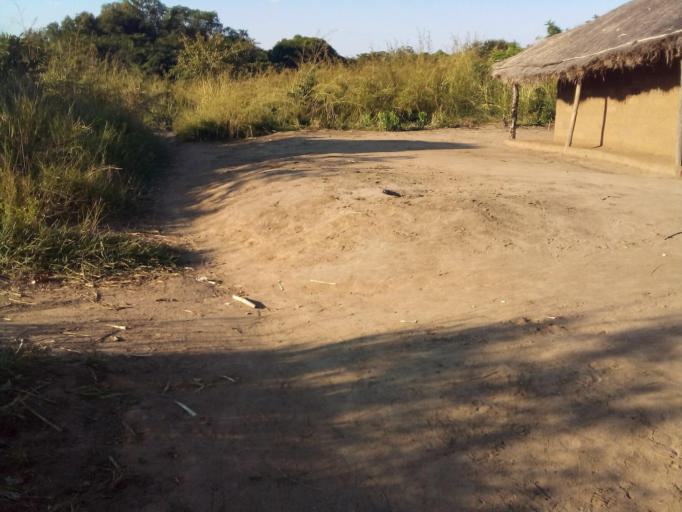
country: MZ
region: Zambezia
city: Quelimane
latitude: -17.4863
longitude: 36.8115
